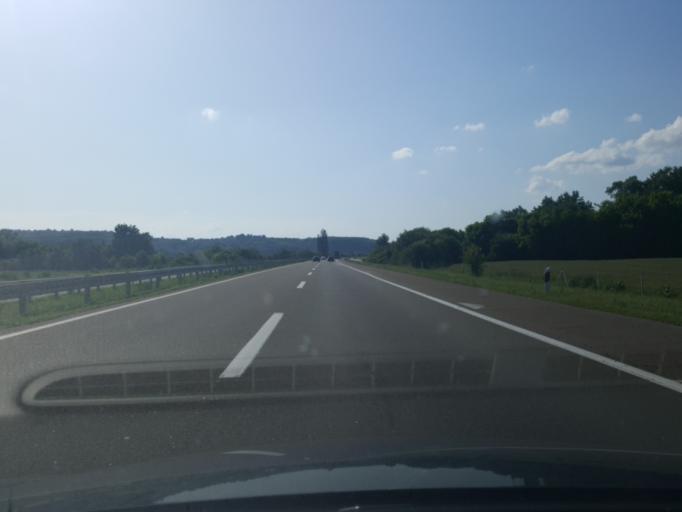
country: RS
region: Central Serbia
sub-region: Sumadijski Okrug
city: Batocina
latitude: 44.1153
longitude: 21.1541
